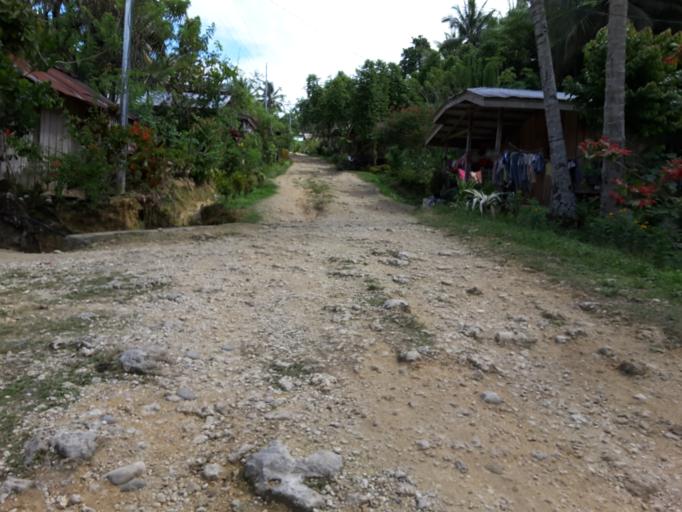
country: PH
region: Caraga
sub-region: Province of Agusan del Sur
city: Bayugan
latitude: 8.7319
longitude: 125.8339
